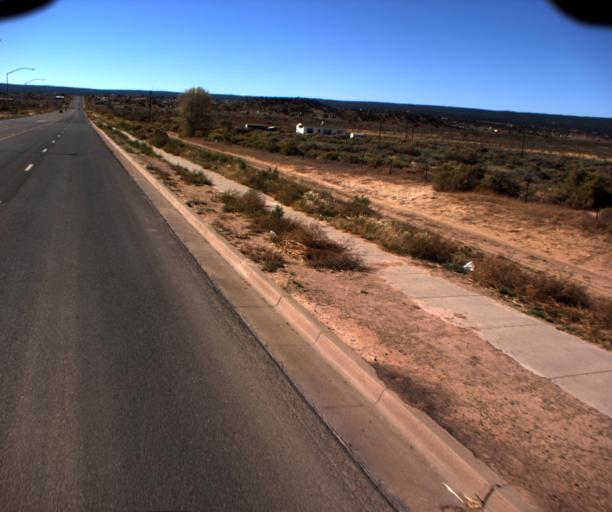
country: US
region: Arizona
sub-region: Apache County
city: Saint Michaels
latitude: 35.6606
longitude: -109.0724
